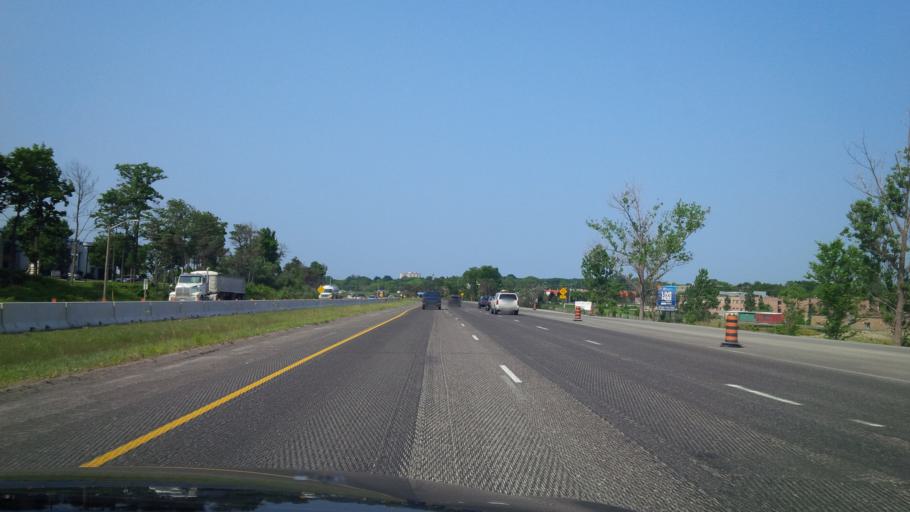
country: CA
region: Ontario
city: Barrie
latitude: 44.4126
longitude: -79.6785
